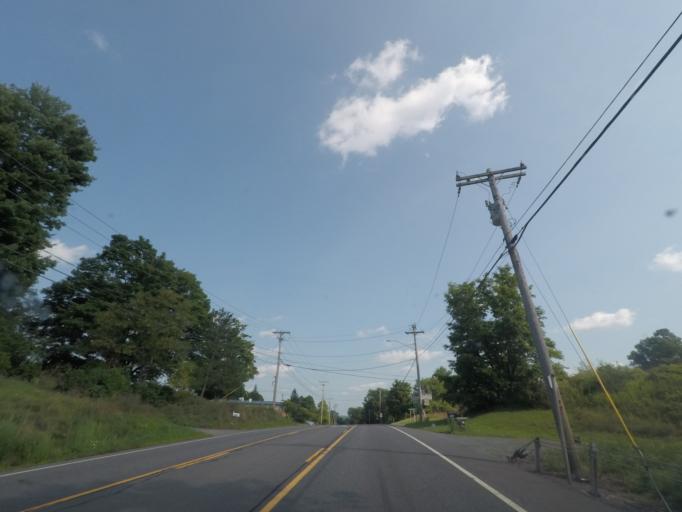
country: US
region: New York
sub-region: Rensselaer County
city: Nassau
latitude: 42.5242
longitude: -73.6422
